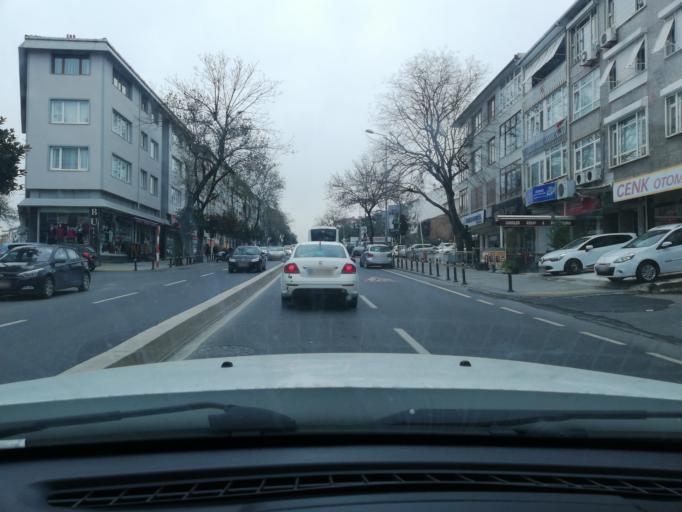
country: TR
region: Istanbul
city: UEskuedar
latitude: 41.0171
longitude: 29.0306
